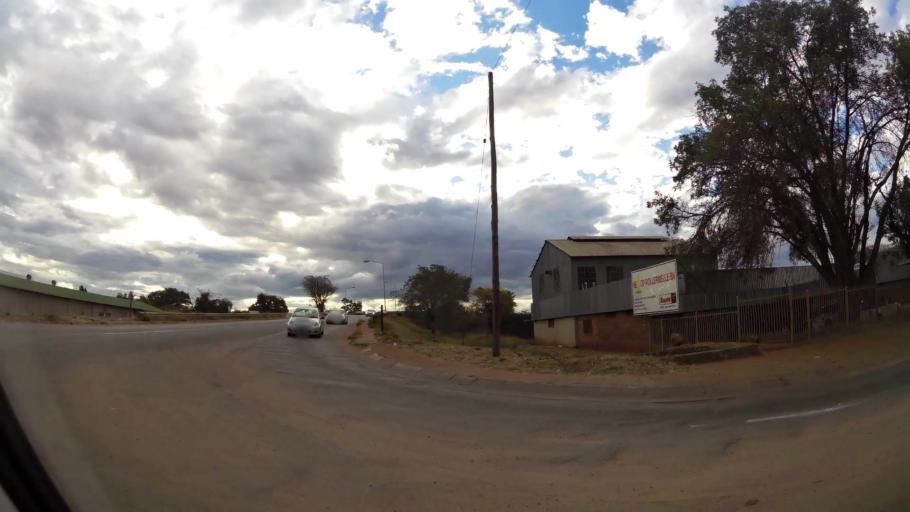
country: ZA
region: Limpopo
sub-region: Waterberg District Municipality
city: Modimolle
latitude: -24.5260
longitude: 28.7110
